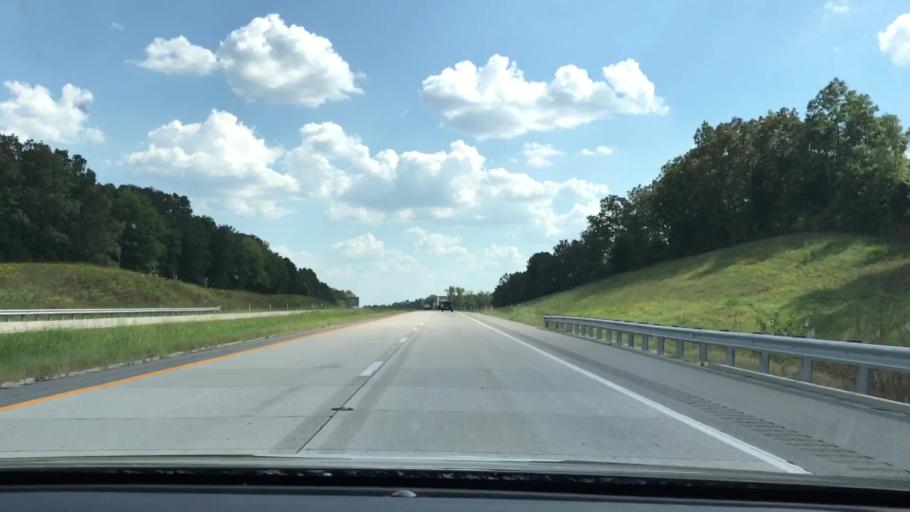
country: US
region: Kentucky
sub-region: Ohio County
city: Oak Grove
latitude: 37.3733
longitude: -86.8026
